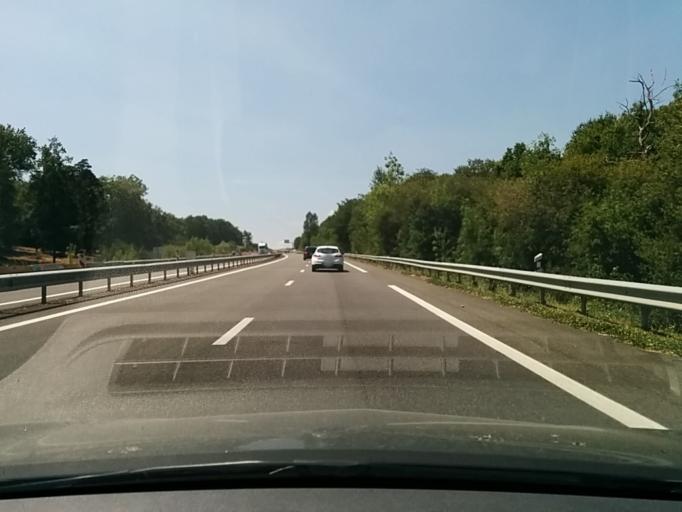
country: FR
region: Midi-Pyrenees
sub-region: Departement du Gers
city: Pujaudran
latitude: 43.5852
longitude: 1.1505
